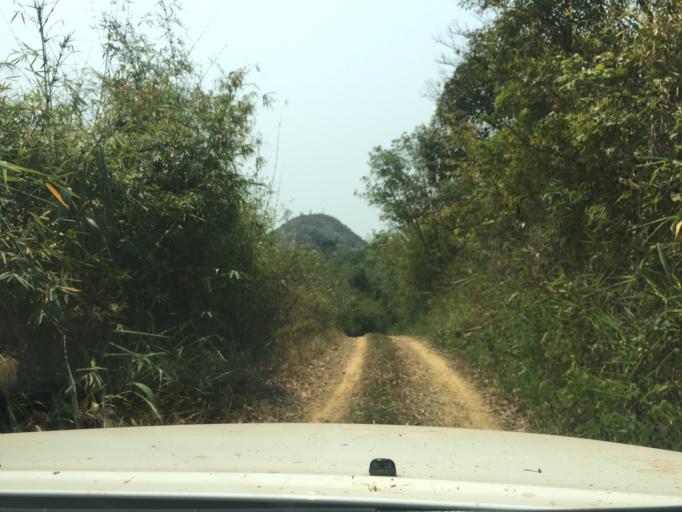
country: LA
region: Loungnamtha
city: Muang Nale
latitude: 20.6256
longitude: 101.6252
